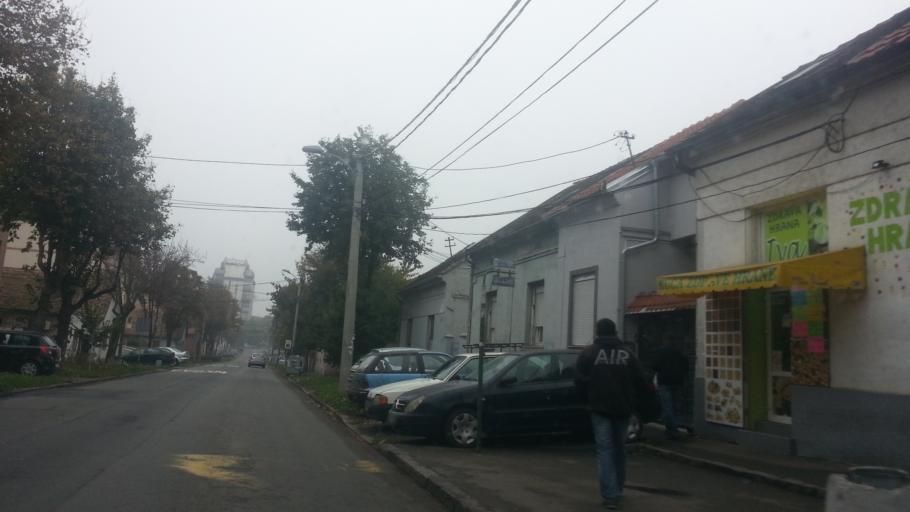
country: RS
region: Central Serbia
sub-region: Belgrade
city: Zemun
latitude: 44.8425
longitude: 20.3848
